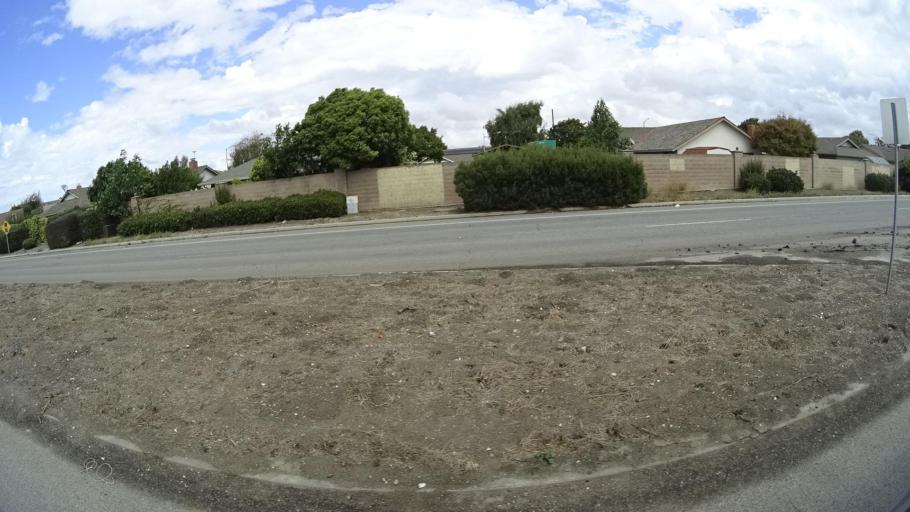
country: US
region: California
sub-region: Monterey County
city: Salinas
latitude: 36.6638
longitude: -121.6817
